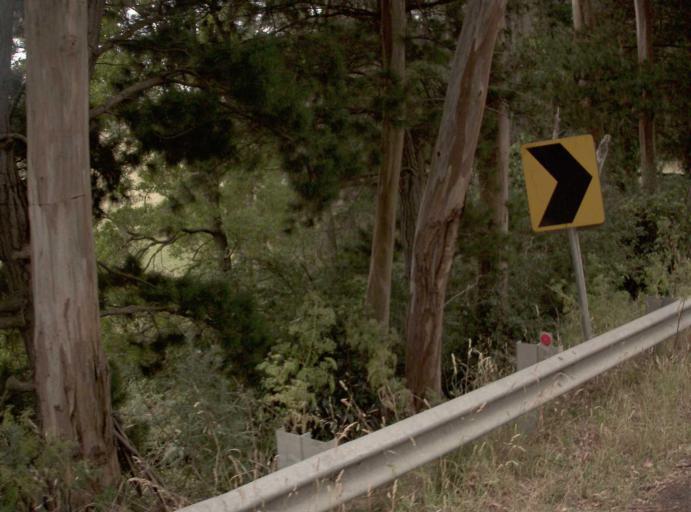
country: AU
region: Victoria
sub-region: Cardinia
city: Bunyip
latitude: -38.1995
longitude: 145.7739
